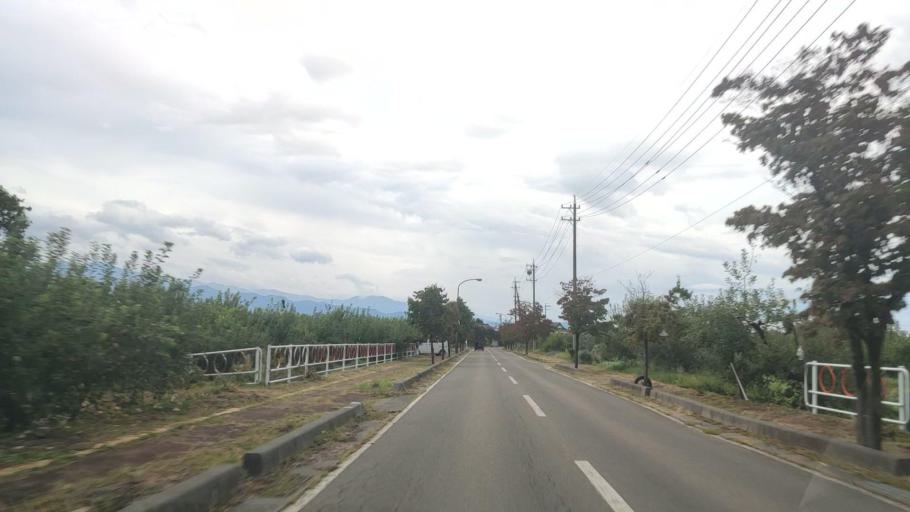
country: JP
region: Nagano
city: Nakano
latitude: 36.7845
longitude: 138.3561
